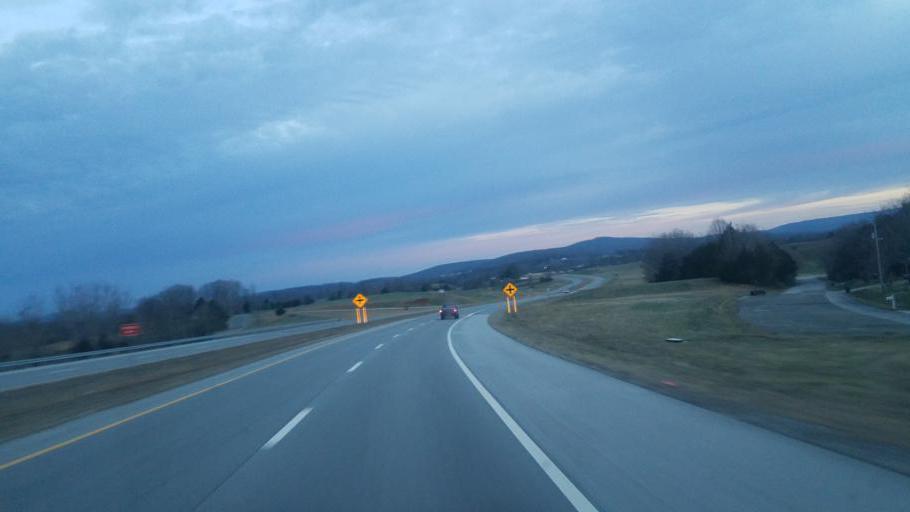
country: US
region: Tennessee
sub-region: Van Buren County
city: Spencer
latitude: 35.7965
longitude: -85.4603
